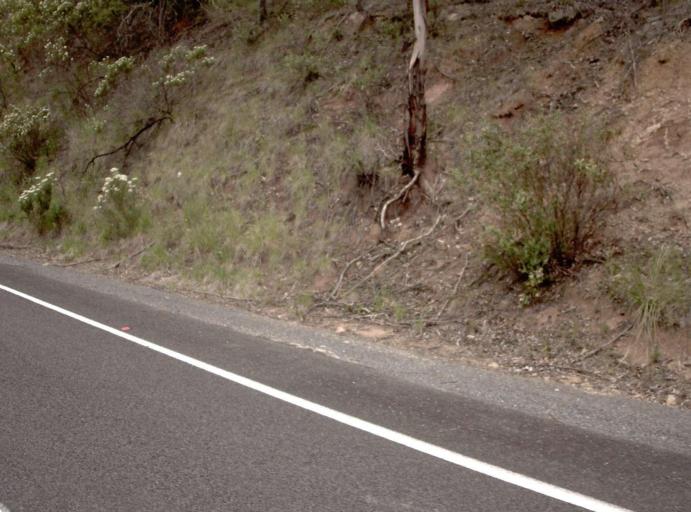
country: AU
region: New South Wales
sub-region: Bombala
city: Bombala
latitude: -37.2560
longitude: 149.2425
